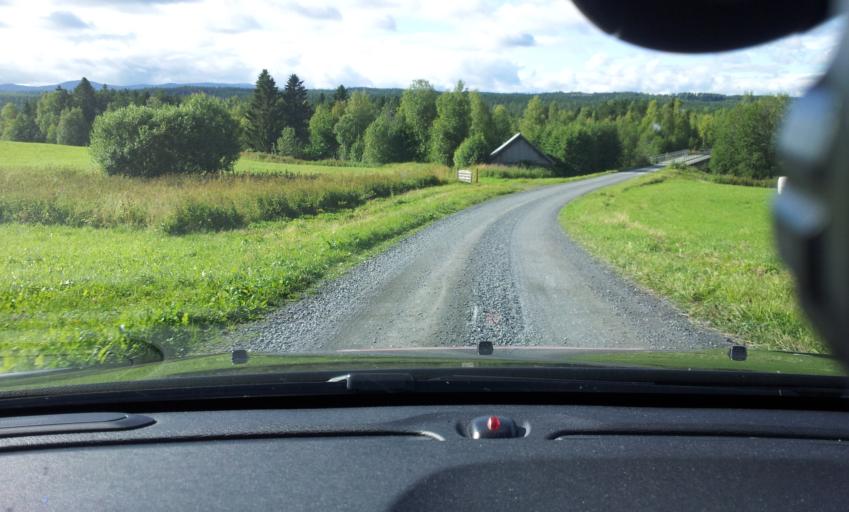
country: SE
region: Jaemtland
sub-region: Krokoms Kommun
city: Valla
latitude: 63.2633
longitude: 13.8366
